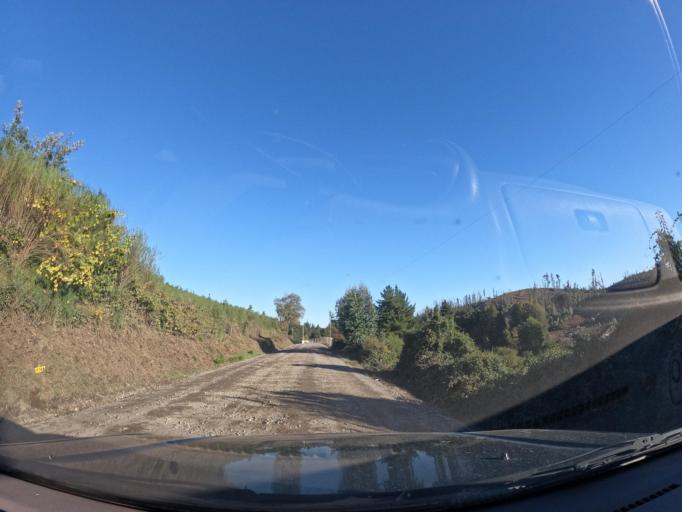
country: CL
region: Biobio
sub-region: Provincia de Concepcion
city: Chiguayante
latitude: -37.0158
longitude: -72.8926
